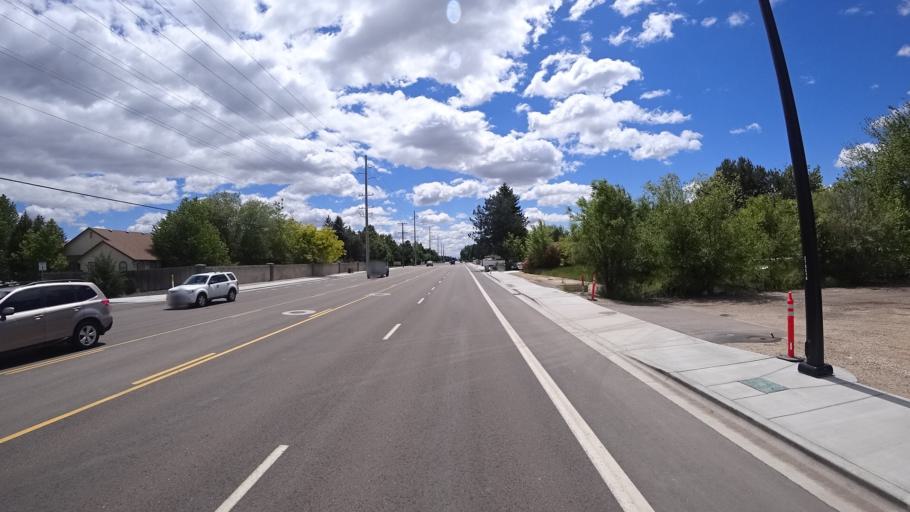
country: US
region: Idaho
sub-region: Ada County
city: Eagle
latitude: 43.6389
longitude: -116.3344
